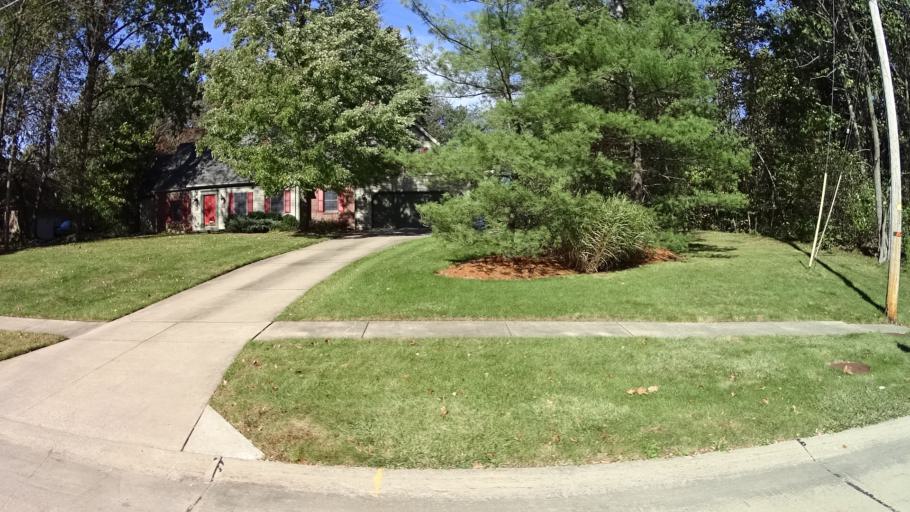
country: US
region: Ohio
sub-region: Lorain County
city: Amherst
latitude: 41.3883
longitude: -82.2434
